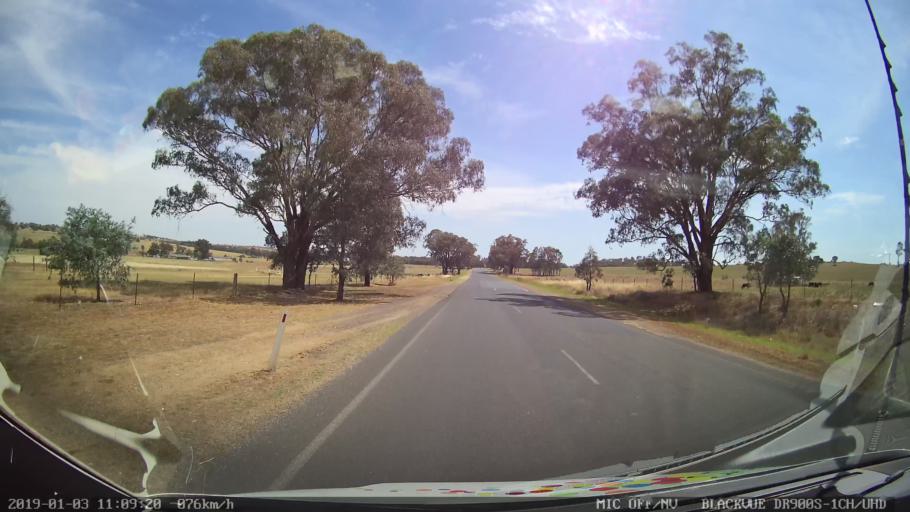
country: AU
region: New South Wales
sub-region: Young
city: Young
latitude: -34.2395
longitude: 148.2554
